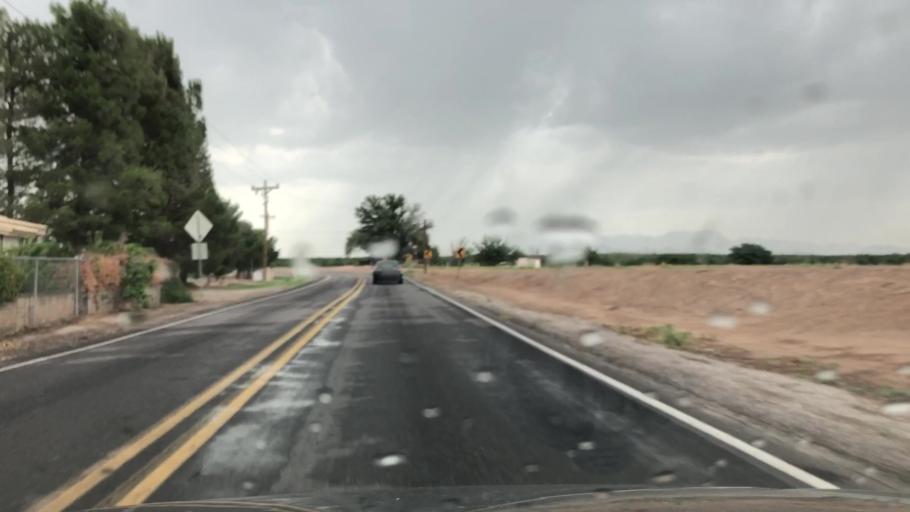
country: US
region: New Mexico
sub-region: Dona Ana County
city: Berino
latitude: 32.0530
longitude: -106.6754
